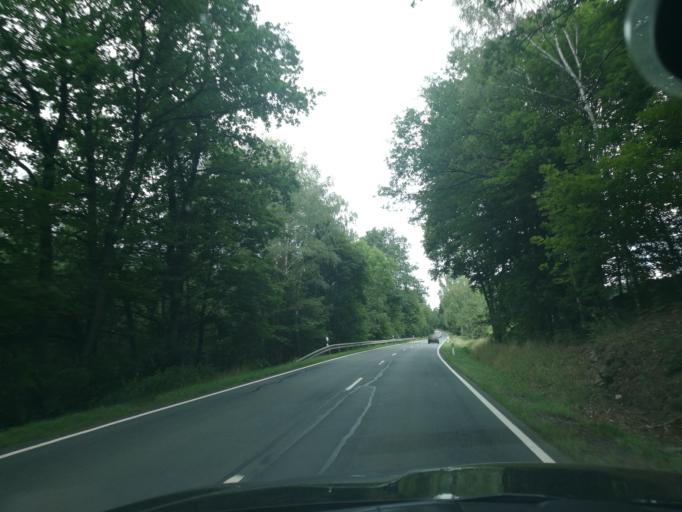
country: DE
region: Saxony
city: Adorf
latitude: 50.3566
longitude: 12.2266
